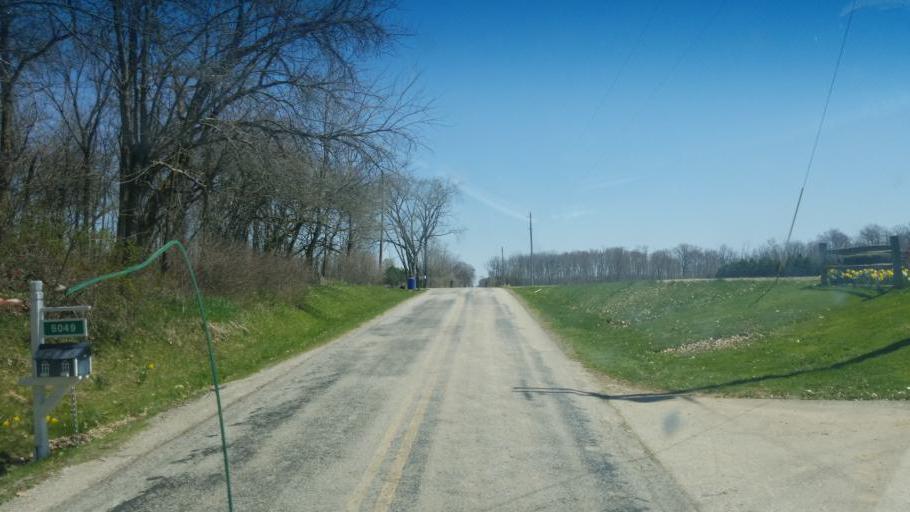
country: US
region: Ohio
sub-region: Huron County
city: New London
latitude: 41.1380
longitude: -82.4054
